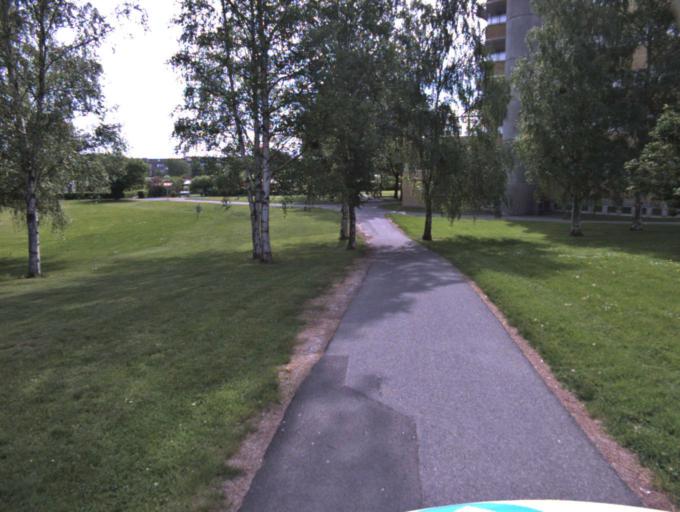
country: SE
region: Skane
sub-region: Kristianstads Kommun
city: Kristianstad
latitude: 56.0316
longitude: 14.1753
